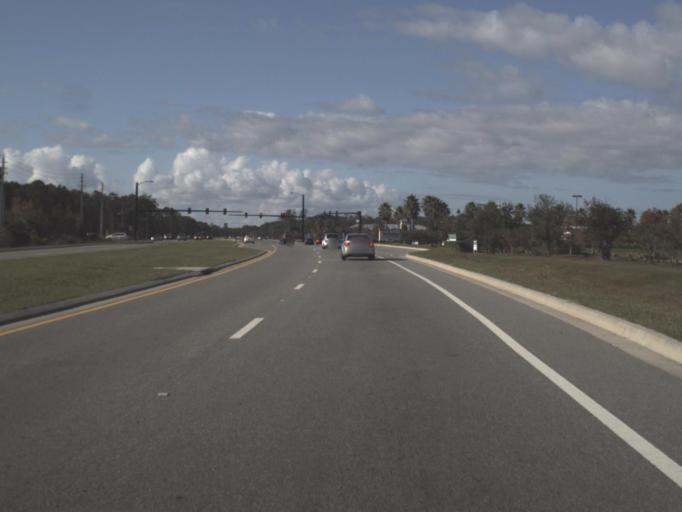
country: US
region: Florida
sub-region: Volusia County
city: Port Orange
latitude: 29.1072
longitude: -81.0333
